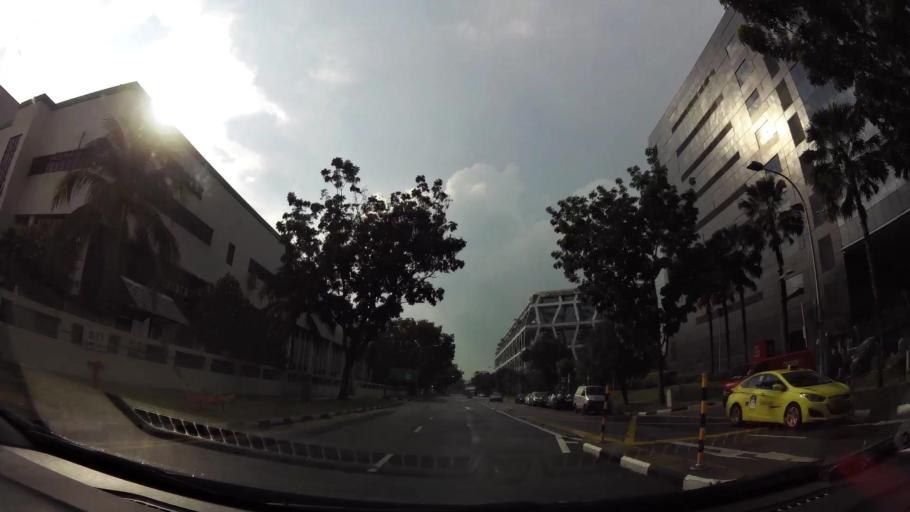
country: SG
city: Singapore
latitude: 1.3322
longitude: 103.9647
